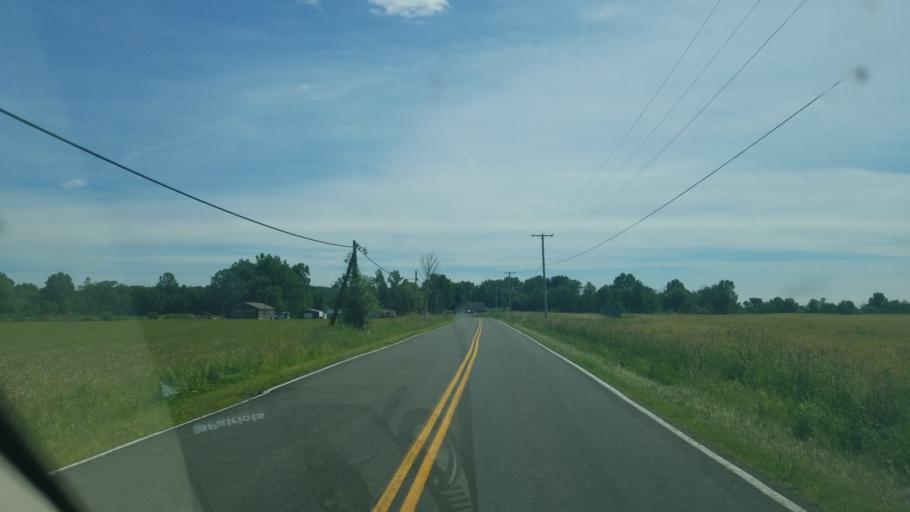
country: US
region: Ohio
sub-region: Stark County
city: Brewster
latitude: 40.7179
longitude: -81.5743
